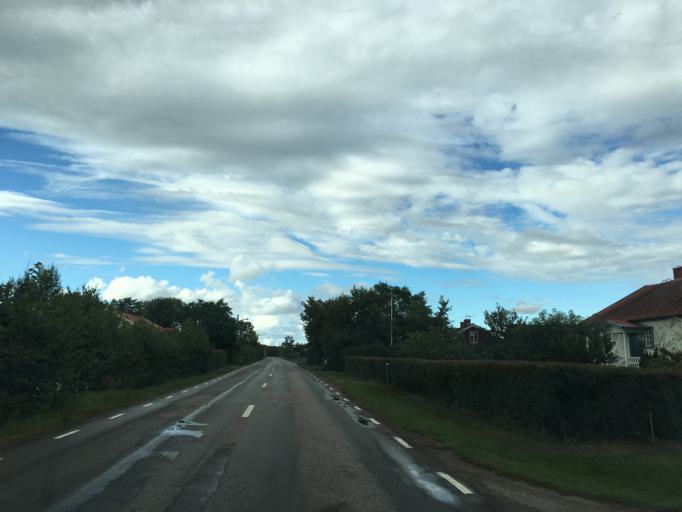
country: SE
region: Kalmar
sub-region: Morbylanga Kommun
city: Moerbylanga
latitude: 56.3659
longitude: 16.4237
